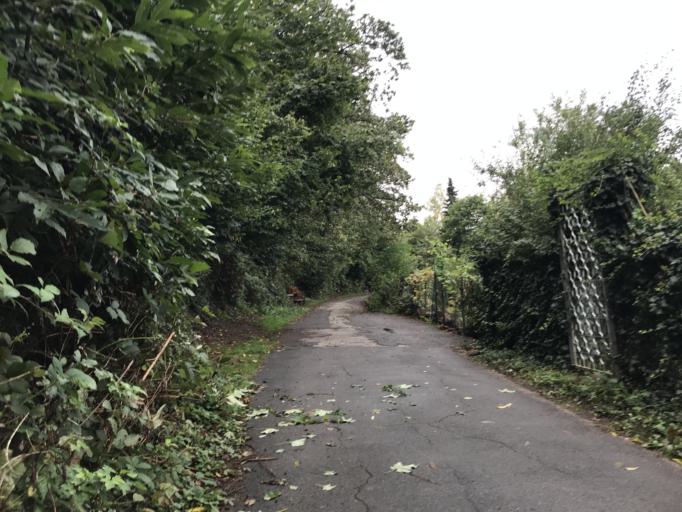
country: DE
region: Baden-Wuerttemberg
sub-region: Karlsruhe Region
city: Heidelberg
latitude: 49.4251
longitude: 8.6965
